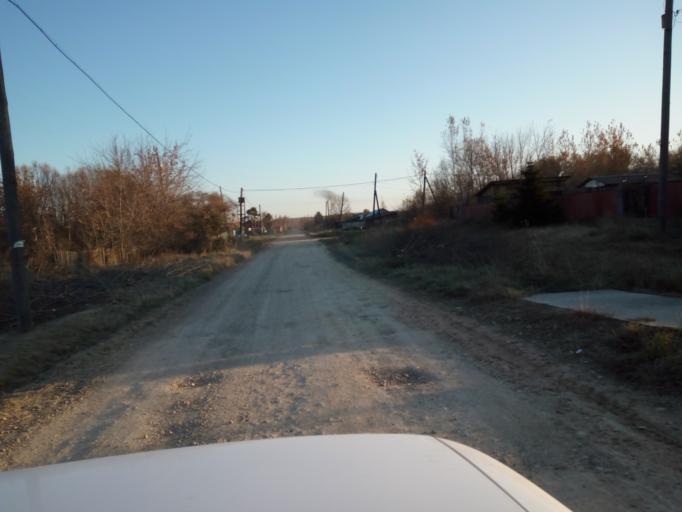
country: RU
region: Primorskiy
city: Lazo
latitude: 45.8783
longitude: 133.6517
